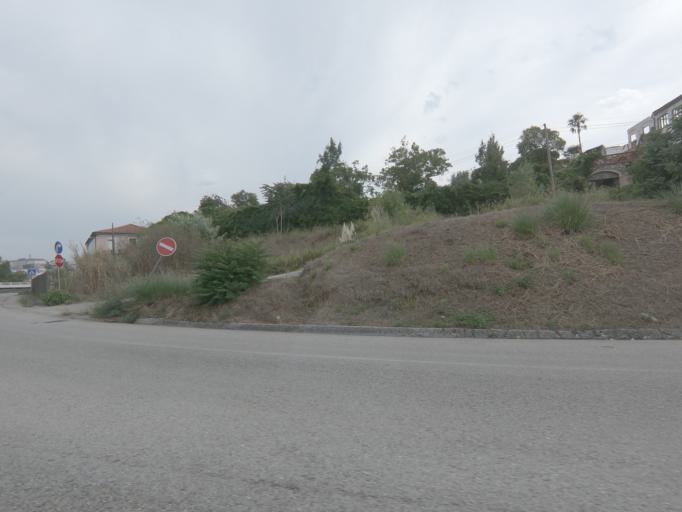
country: PT
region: Coimbra
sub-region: Coimbra
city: Coimbra
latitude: 40.2148
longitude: -8.4432
